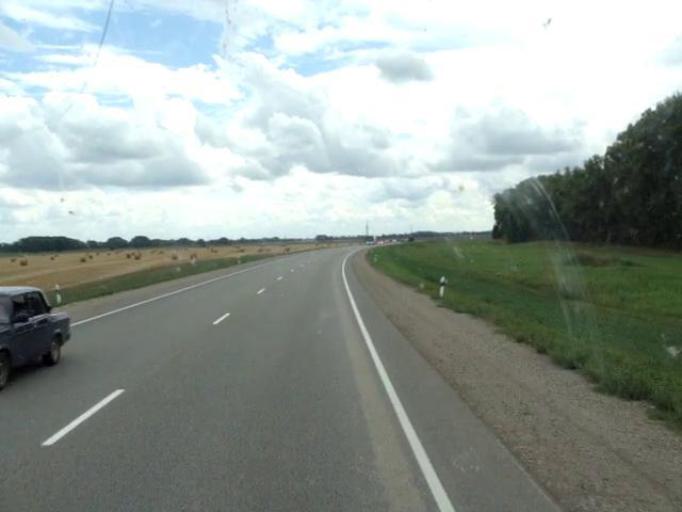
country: RU
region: Altai Krai
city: Shubenka
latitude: 52.6833
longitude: 85.0450
